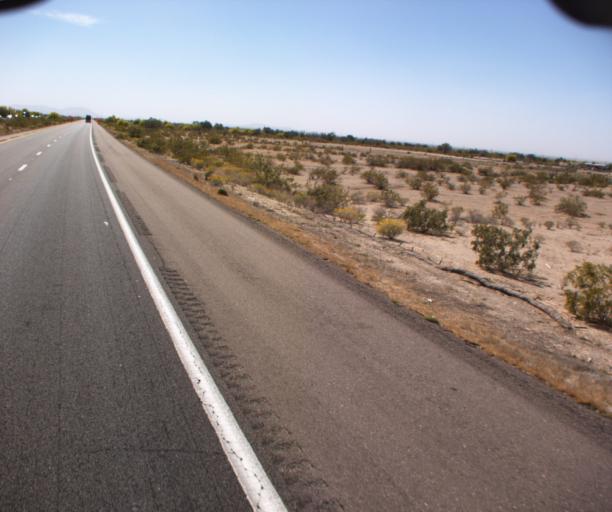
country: US
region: Arizona
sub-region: Maricopa County
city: Gila Bend
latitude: 33.0171
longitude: -112.6515
